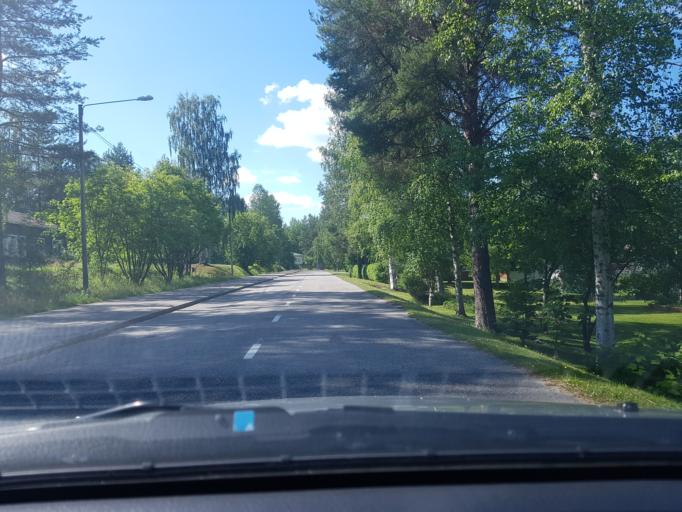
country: FI
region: Kainuu
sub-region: Kehys-Kainuu
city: Kuhmo
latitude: 64.1220
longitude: 29.5219
